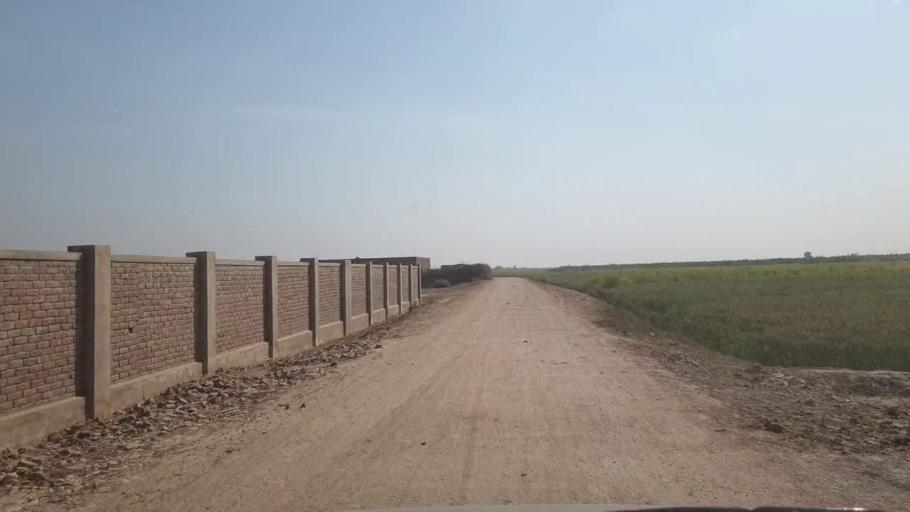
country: PK
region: Sindh
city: Chambar
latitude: 25.3747
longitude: 68.8080
